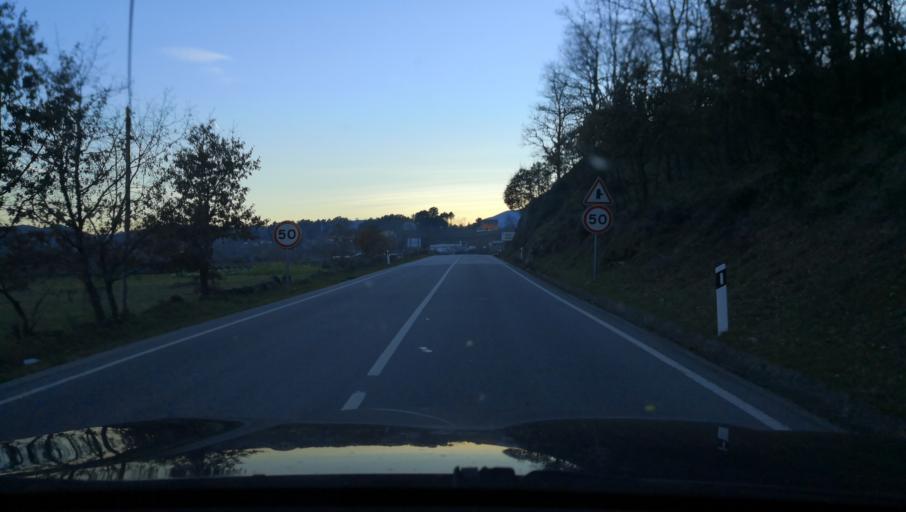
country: PT
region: Vila Real
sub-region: Vila Pouca de Aguiar
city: Vila Pouca de Aguiar
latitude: 41.4279
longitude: -7.6821
